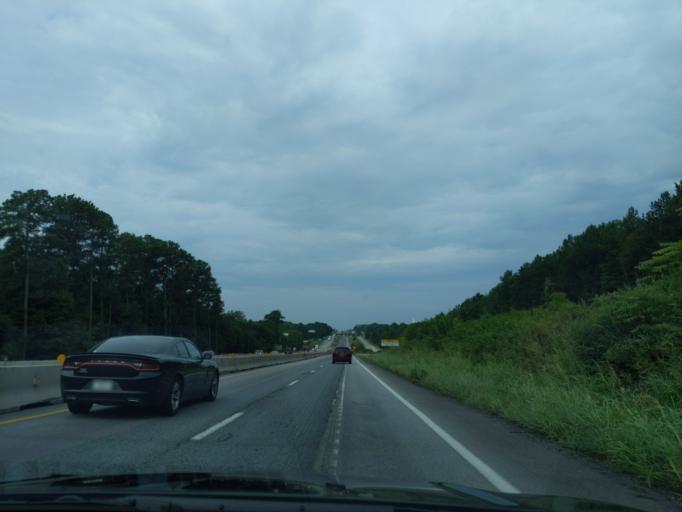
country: US
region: South Carolina
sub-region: Spartanburg County
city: Cowpens
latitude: 35.0343
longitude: -81.8452
